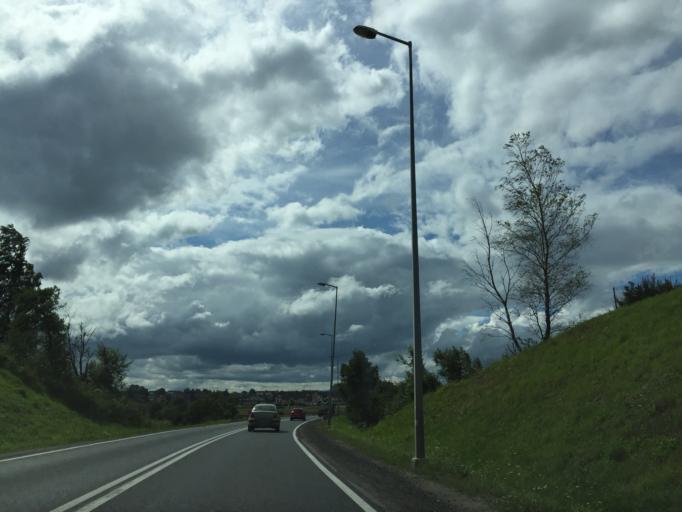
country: PL
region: Lesser Poland Voivodeship
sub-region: Powiat nowotarski
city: Nowy Targ
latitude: 49.4755
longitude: 20.0452
